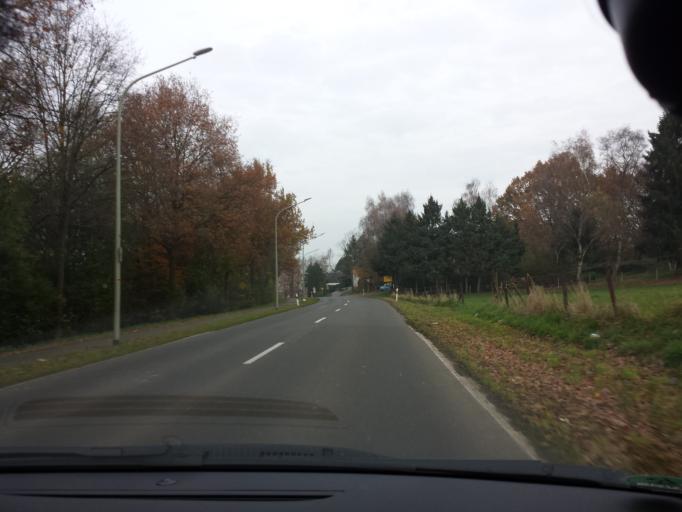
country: DE
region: North Rhine-Westphalia
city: Geilenkirchen
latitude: 50.9754
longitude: 6.0779
